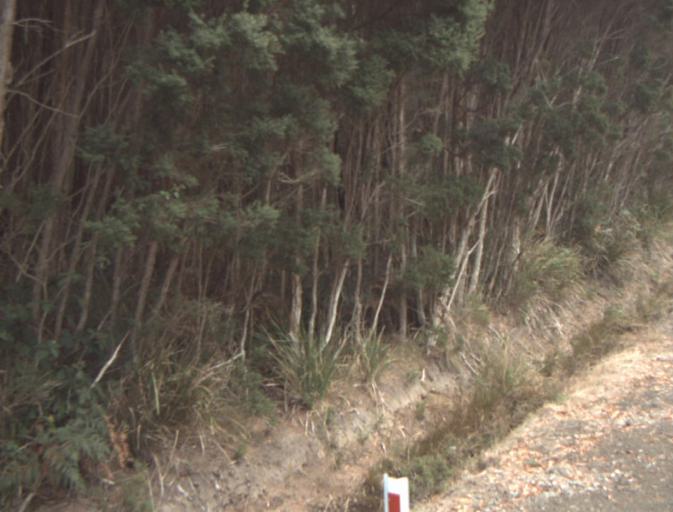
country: AU
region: Tasmania
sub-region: Launceston
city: Mayfield
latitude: -41.2823
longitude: 147.0286
